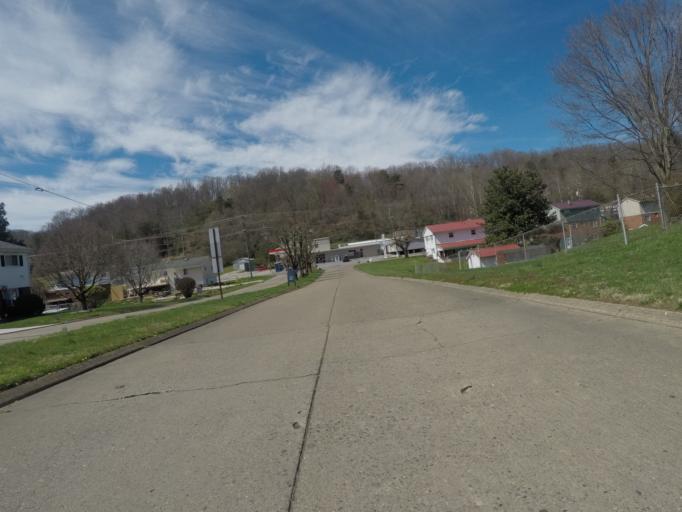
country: US
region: West Virginia
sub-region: Cabell County
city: Pea Ridge
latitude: 38.4035
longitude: -82.3188
